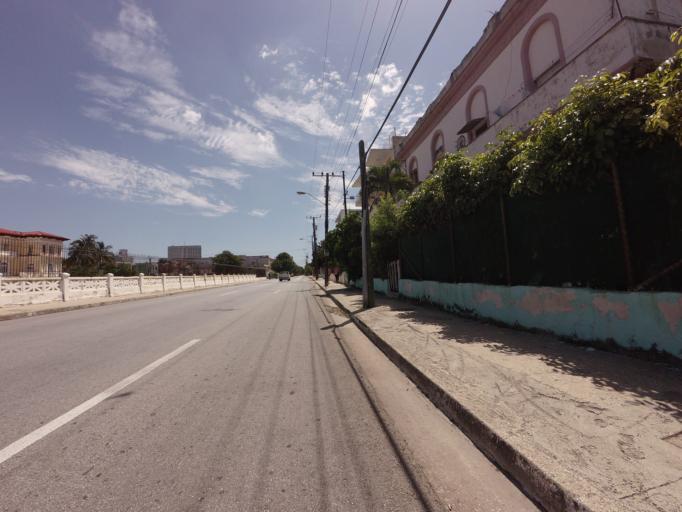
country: CU
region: La Habana
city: Havana
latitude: 23.1333
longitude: -82.4065
